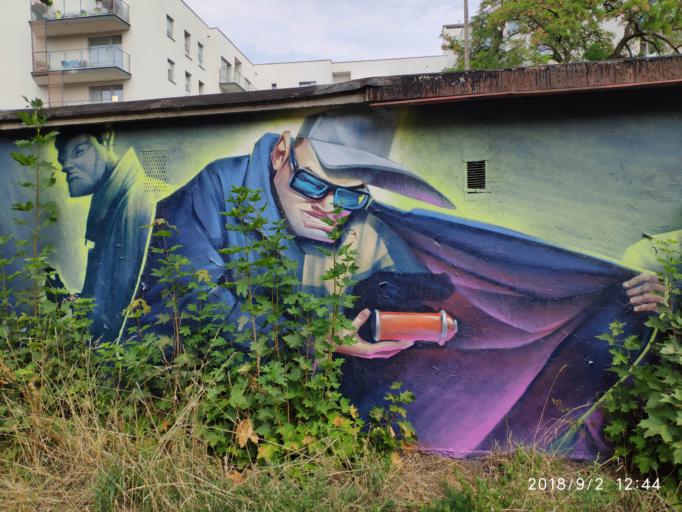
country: PL
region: Lubusz
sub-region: Zielona Gora
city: Zielona Gora
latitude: 51.9326
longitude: 15.5001
